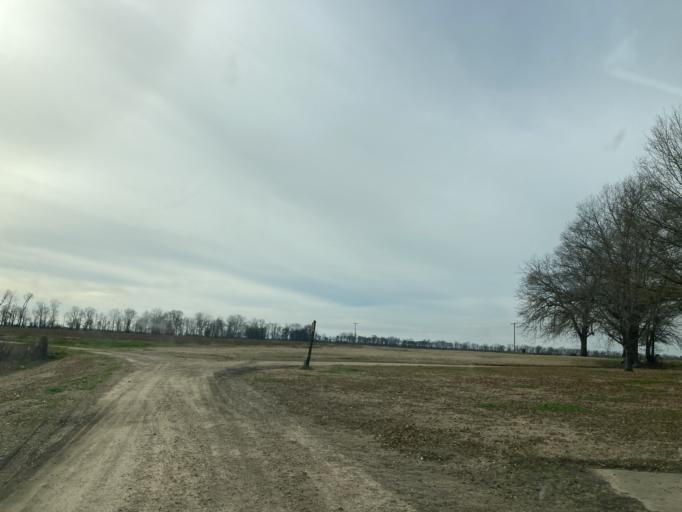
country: US
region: Mississippi
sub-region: Humphreys County
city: Belzoni
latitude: 33.1222
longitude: -90.6163
